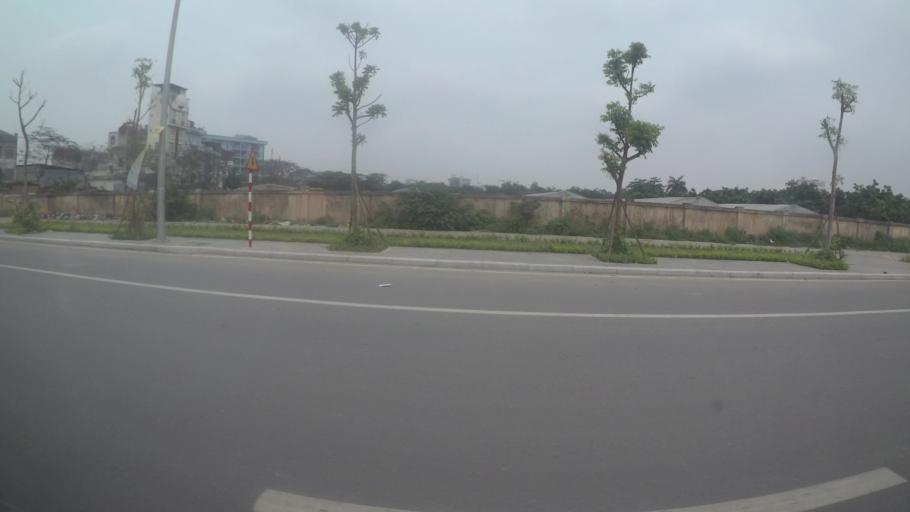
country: VN
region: Ha Noi
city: Cau Dien
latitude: 21.0470
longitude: 105.7361
